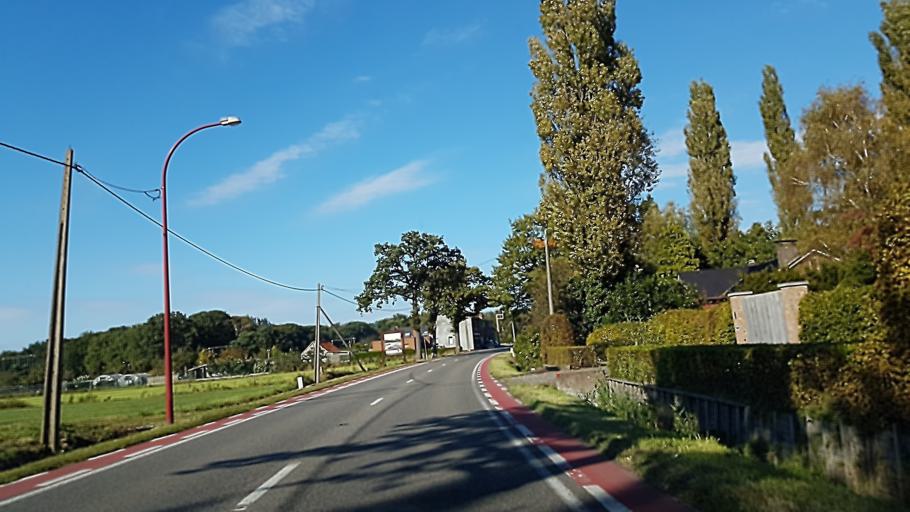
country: BE
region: Flanders
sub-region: Provincie Antwerpen
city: Kalmthout
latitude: 51.4021
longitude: 4.4683
